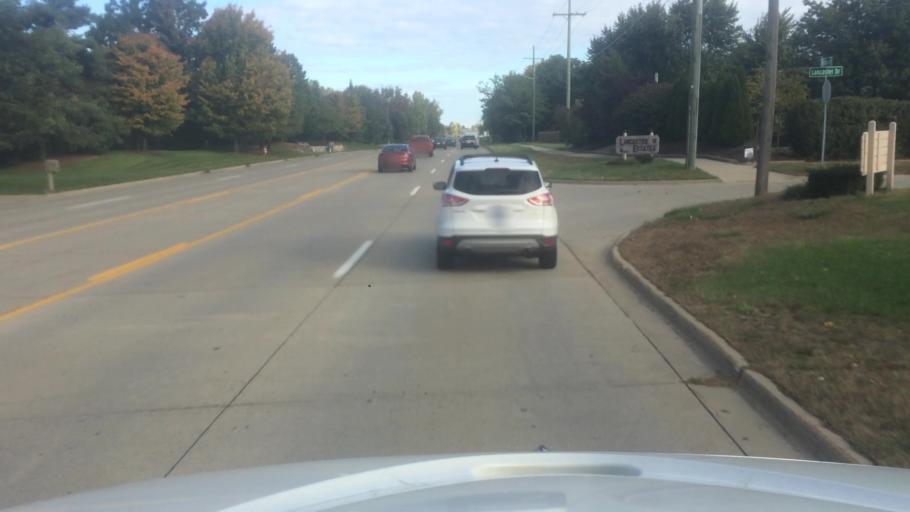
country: US
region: Michigan
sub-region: Macomb County
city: Shelby
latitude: 42.6597
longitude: -82.9942
